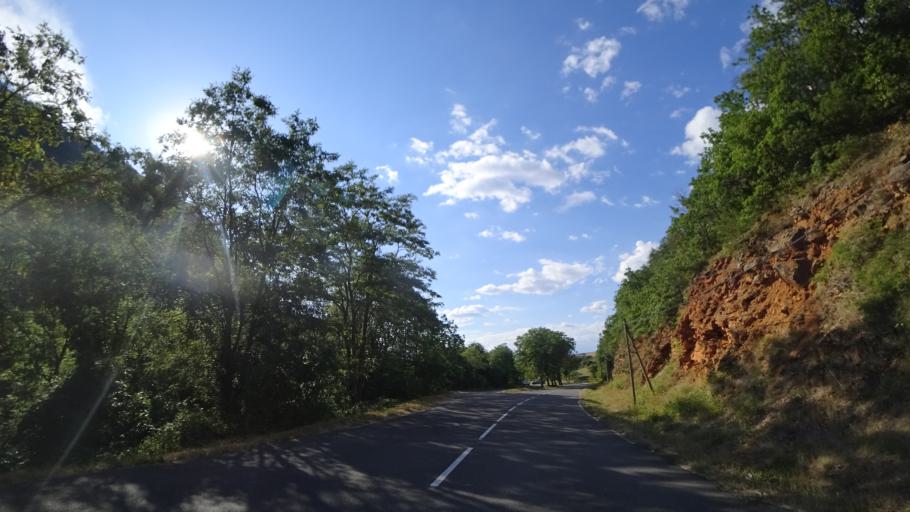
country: FR
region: Languedoc-Roussillon
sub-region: Departement de la Lozere
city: La Canourgue
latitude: 44.4124
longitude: 3.2361
